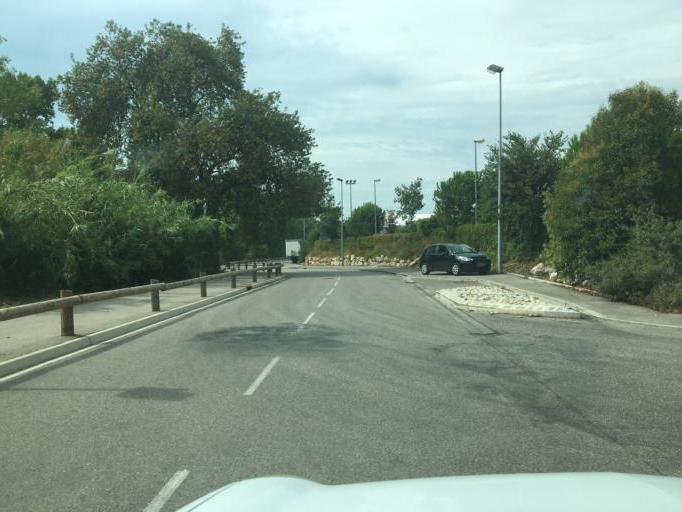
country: FR
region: Provence-Alpes-Cote d'Azur
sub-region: Departement des Bouches-du-Rhone
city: Bouc-Bel-Air
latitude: 43.4817
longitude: 5.3934
